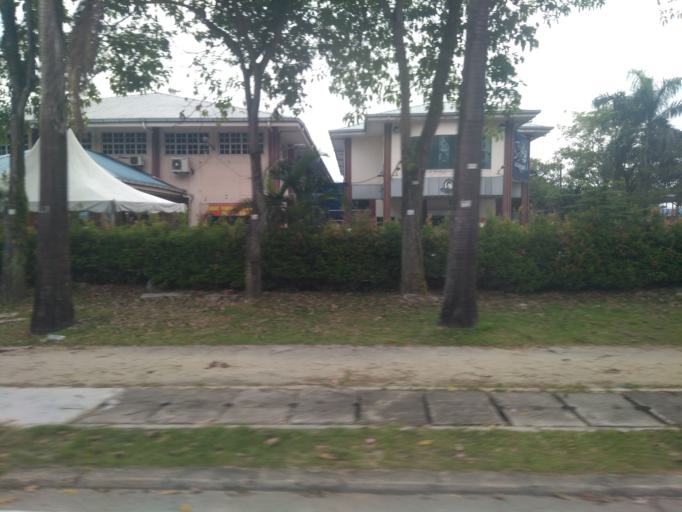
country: MY
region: Johor
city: Johor Bahru
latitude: 1.4949
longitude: 103.7034
